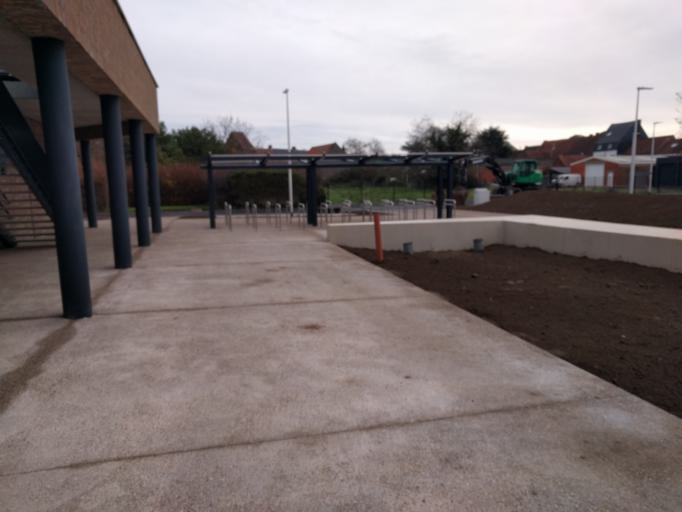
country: BE
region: Flanders
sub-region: Provincie West-Vlaanderen
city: Wevelgem
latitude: 50.8077
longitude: 3.1743
